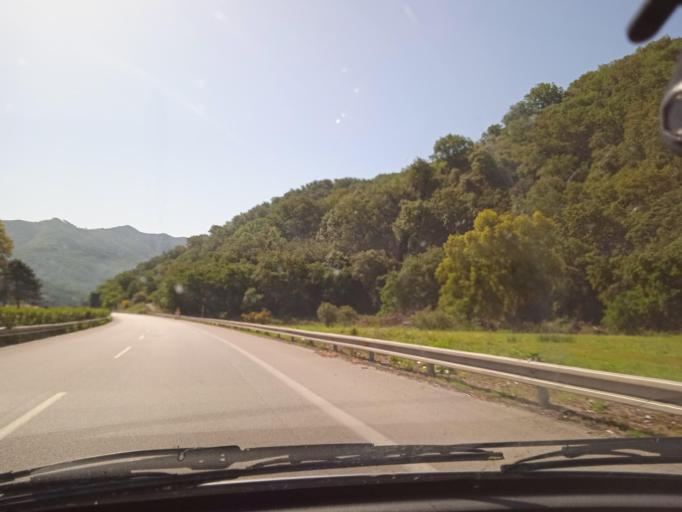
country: IT
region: Sicily
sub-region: Messina
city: Piraino
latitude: 38.1464
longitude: 14.8570
